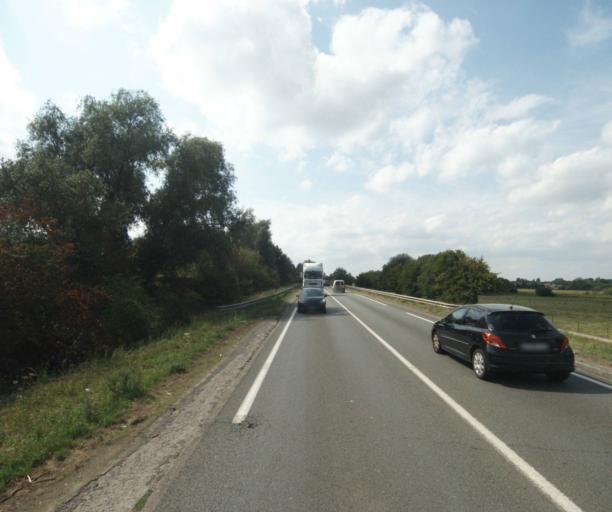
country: FR
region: Nord-Pas-de-Calais
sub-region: Departement du Nord
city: Hem
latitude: 50.6480
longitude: 3.1838
